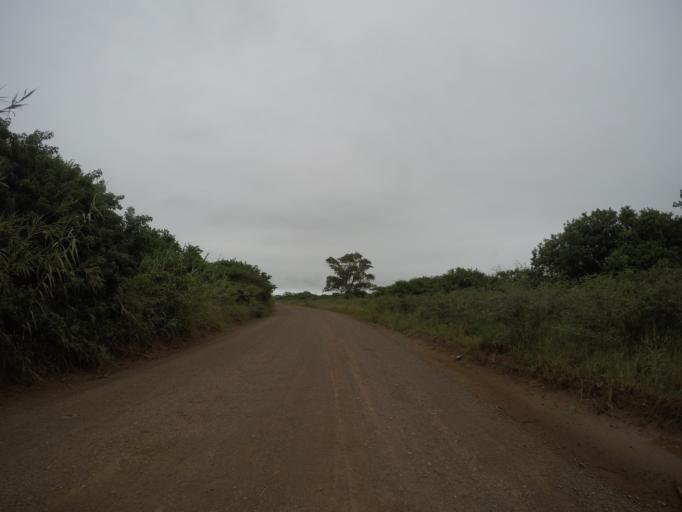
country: ZA
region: KwaZulu-Natal
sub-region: uThungulu District Municipality
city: Empangeni
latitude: -28.6568
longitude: 31.7874
